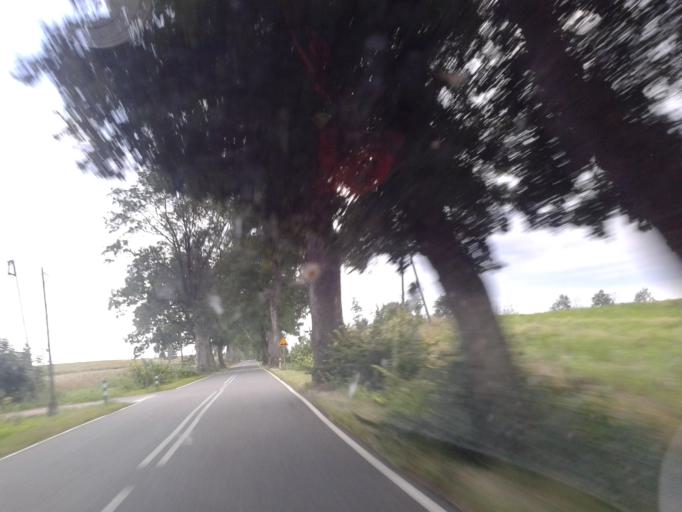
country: PL
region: West Pomeranian Voivodeship
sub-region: Powiat szczecinecki
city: Grzmiaca
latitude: 53.8780
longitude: 16.4966
